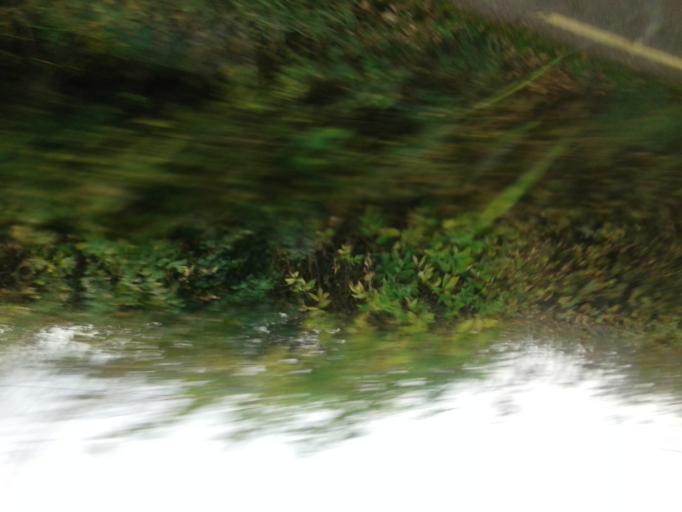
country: IE
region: Munster
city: Nenagh Bridge
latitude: 52.9360
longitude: -8.0419
